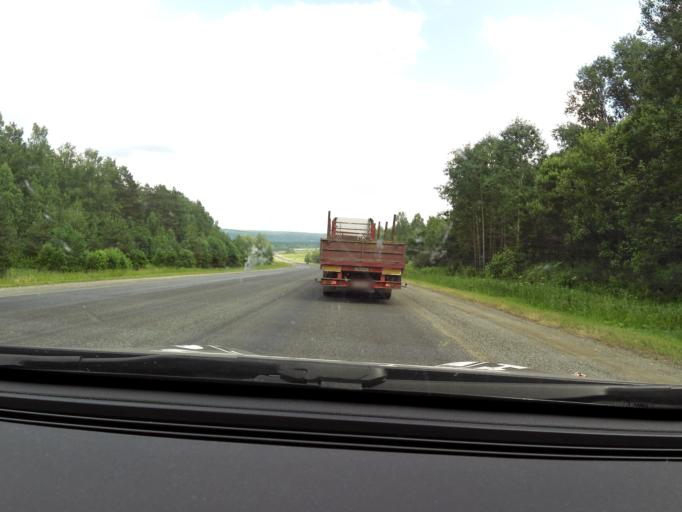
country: RU
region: Sverdlovsk
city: Ufimskiy
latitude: 56.7871
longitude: 58.3220
